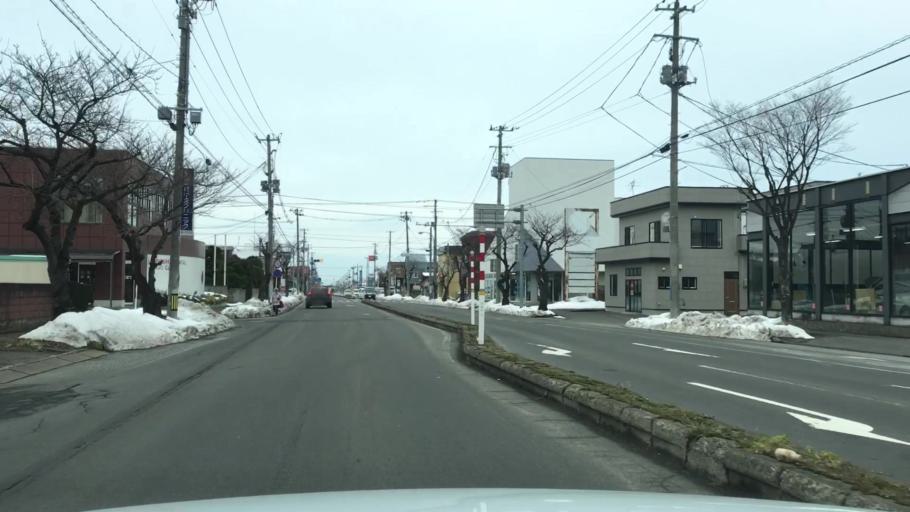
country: JP
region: Aomori
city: Hirosaki
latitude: 40.5958
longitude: 140.4926
